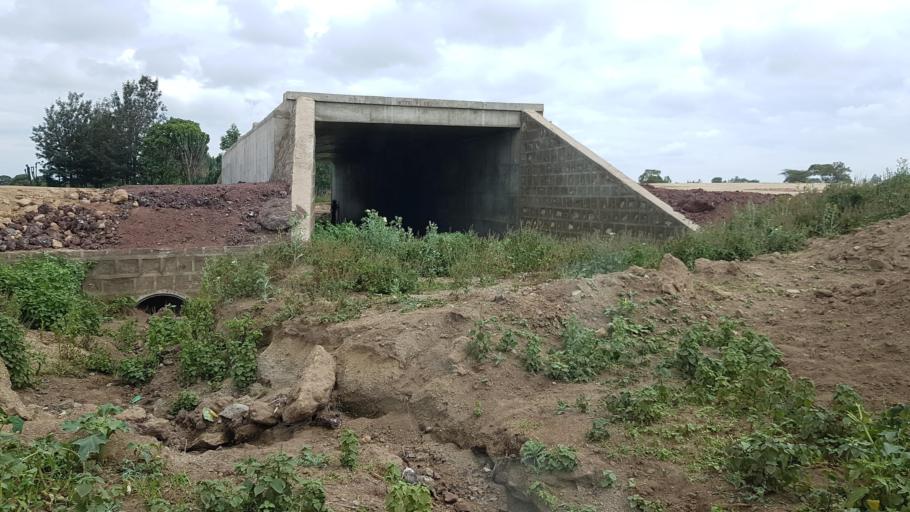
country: ET
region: Oromiya
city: Shashemene
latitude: 7.2435
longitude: 38.5844
